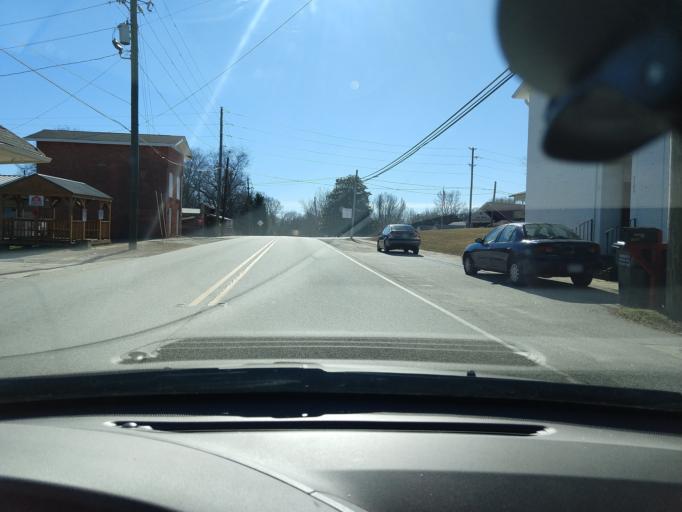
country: US
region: Georgia
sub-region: Walton County
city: Social Circle
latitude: 33.5178
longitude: -83.7342
